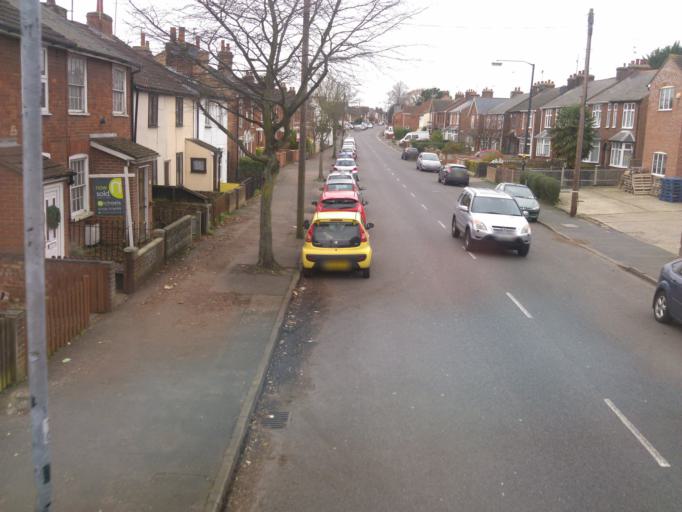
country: GB
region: England
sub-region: Essex
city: Colchester
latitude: 51.8883
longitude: 0.9255
